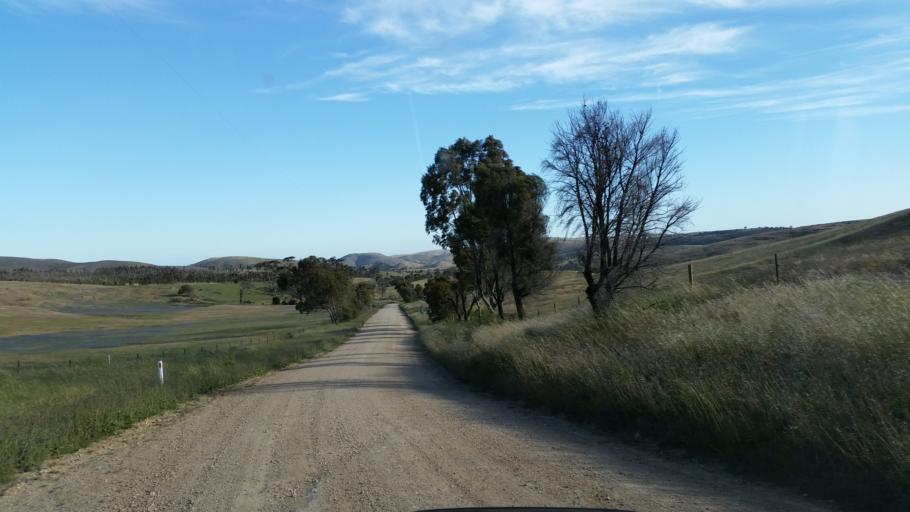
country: AU
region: South Australia
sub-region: Barossa
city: Angaston
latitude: -34.6874
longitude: 139.1682
